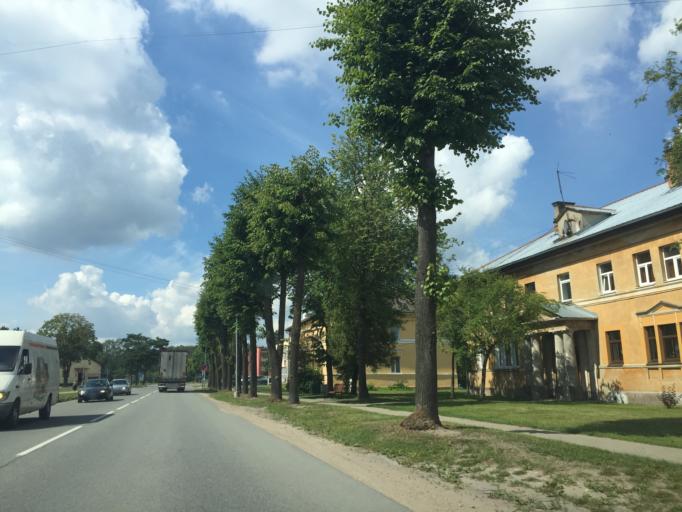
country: LV
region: Kekava
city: Balozi
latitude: 56.8756
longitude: 24.1209
